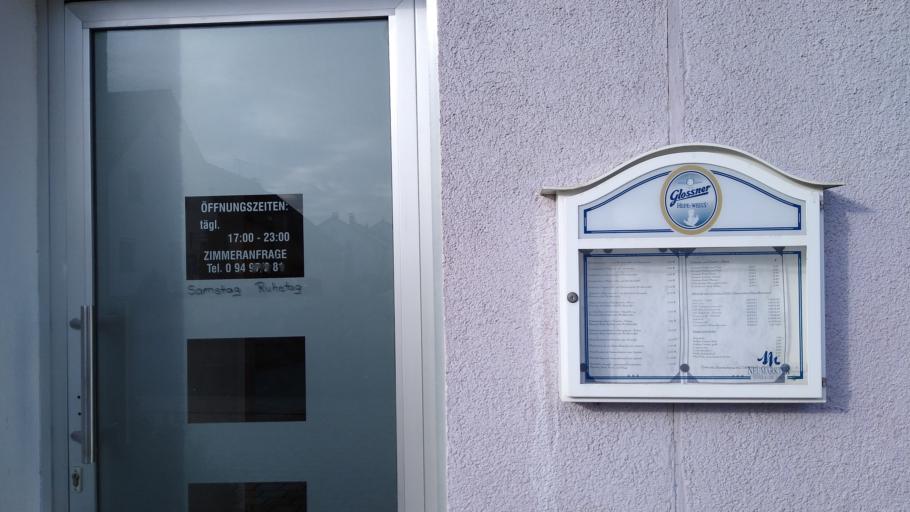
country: DE
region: Bavaria
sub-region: Upper Palatinate
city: Seubersdorf
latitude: 49.1648
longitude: 11.6255
